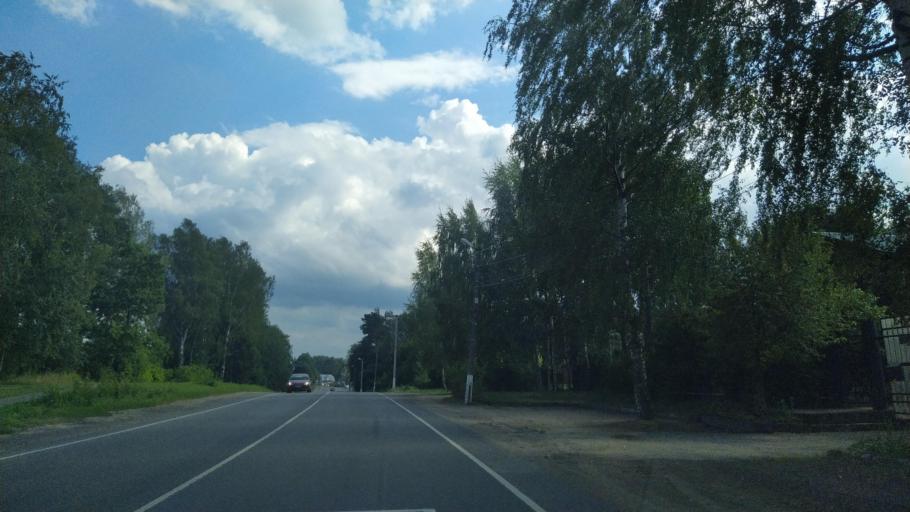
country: RU
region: Leningrad
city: Toksovo
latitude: 60.1464
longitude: 30.5239
